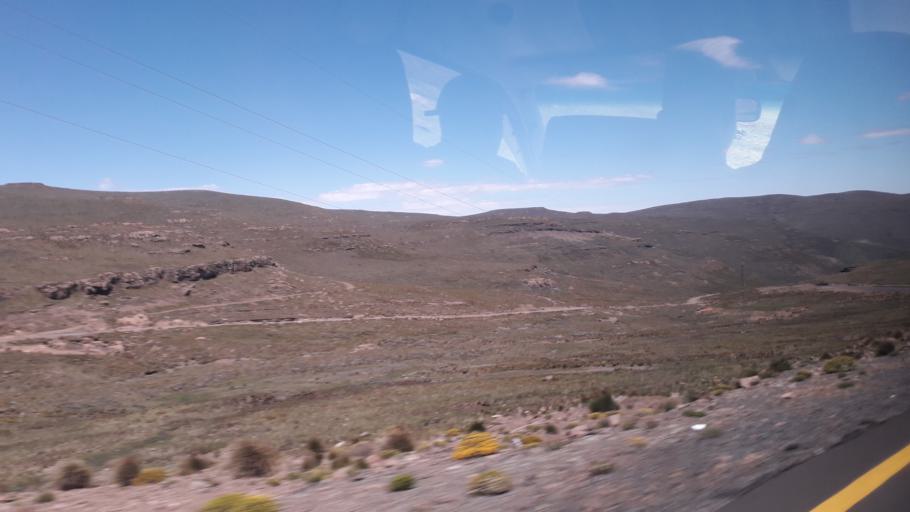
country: ZA
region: Orange Free State
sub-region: Thabo Mofutsanyana District Municipality
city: Phuthaditjhaba
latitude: -28.8102
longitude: 28.7111
